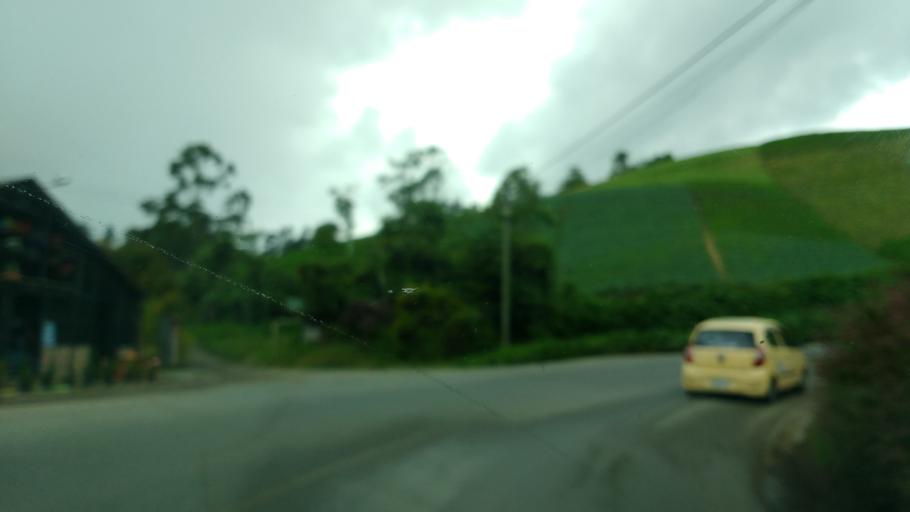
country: CO
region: Antioquia
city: Marinilla
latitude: 6.1758
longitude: -75.3171
